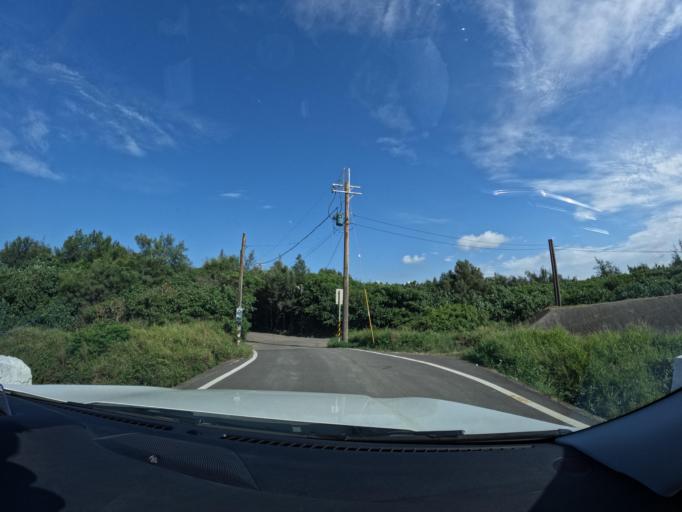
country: TW
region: Taiwan
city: Taoyuan City
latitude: 25.0871
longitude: 121.1773
